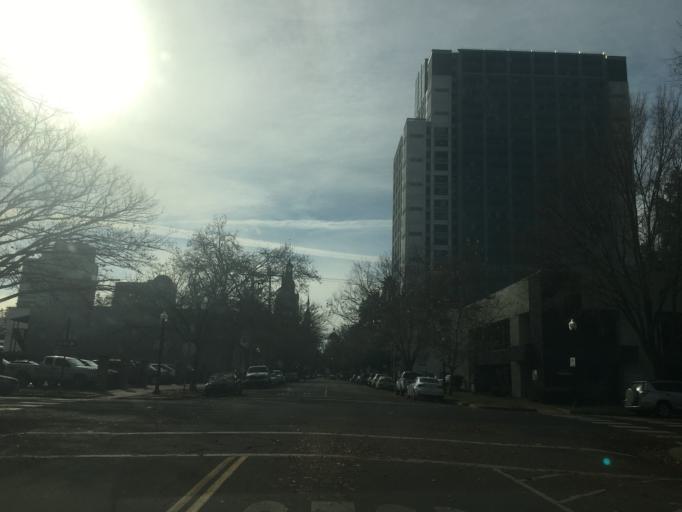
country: US
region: California
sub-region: Sacramento County
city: Sacramento
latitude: 38.5835
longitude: -121.4905
